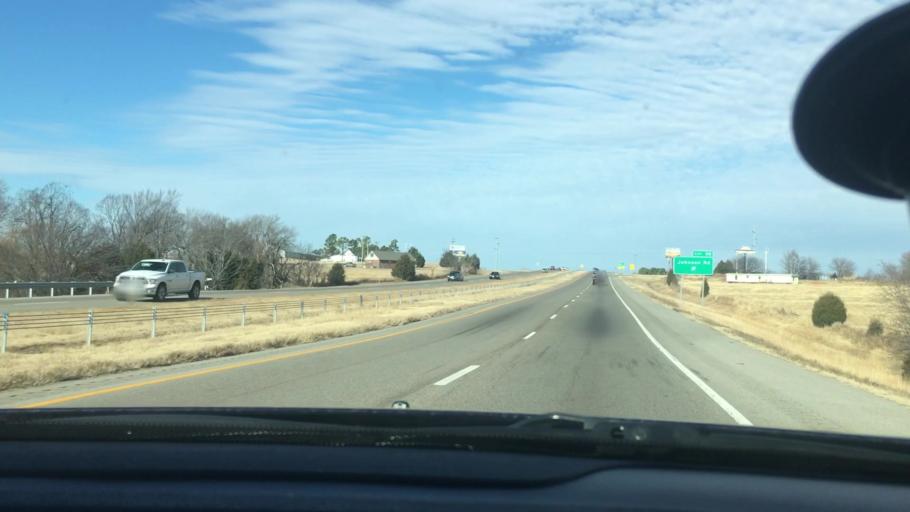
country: US
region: Oklahoma
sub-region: Cleveland County
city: Noble
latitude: 35.0746
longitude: -97.4034
